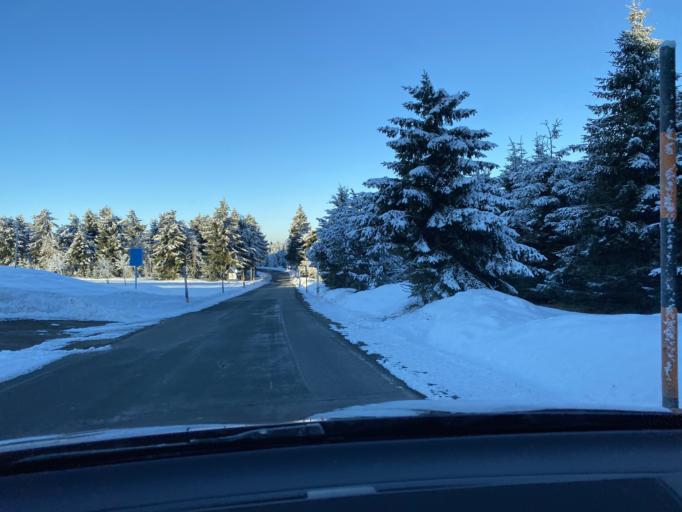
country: DE
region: Saxony
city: Kurort Oberwiesenthal
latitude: 50.4190
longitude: 12.9395
